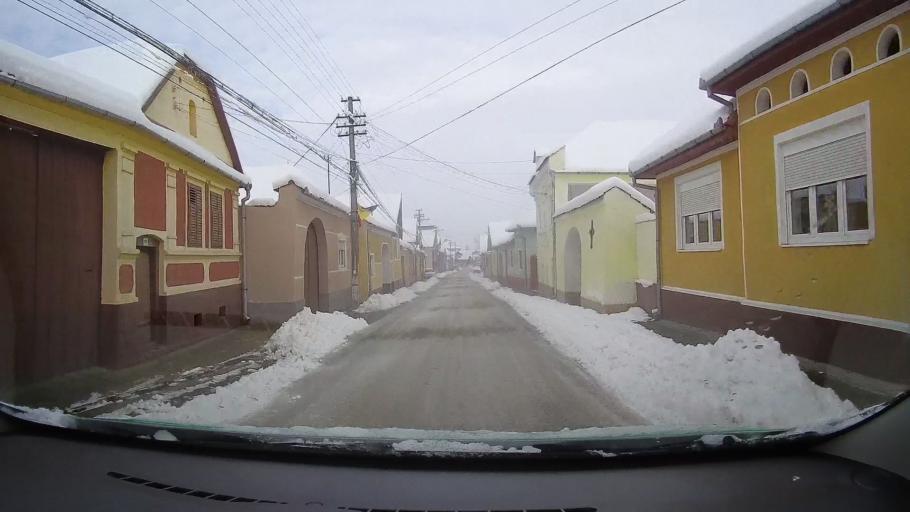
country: RO
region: Alba
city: Pianu de Sus
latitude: 45.8928
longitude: 23.4837
